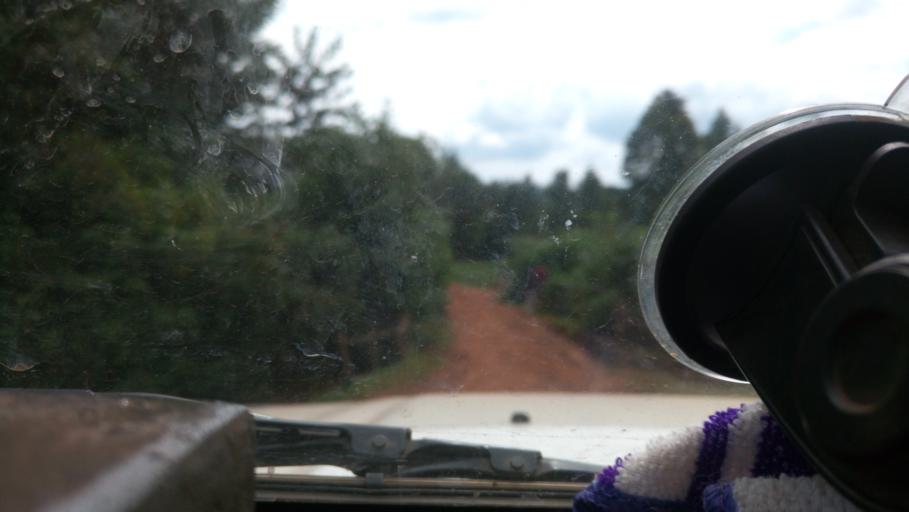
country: KE
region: Kericho
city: Litein
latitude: -0.4180
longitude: 35.0973
